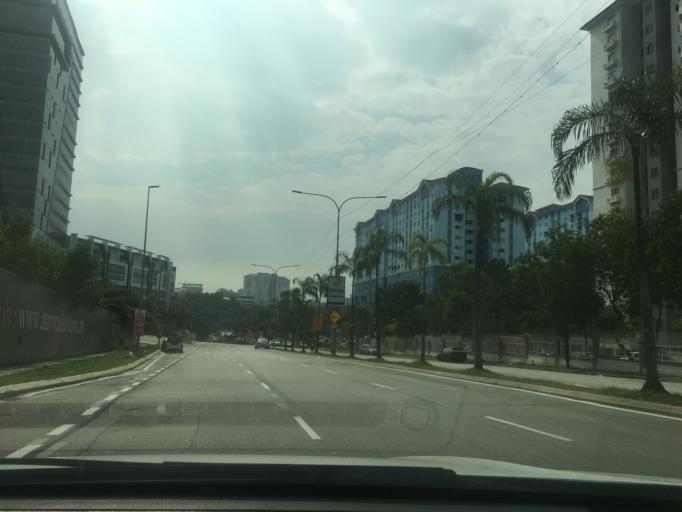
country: MY
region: Selangor
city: Kampong Baharu Balakong
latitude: 3.0550
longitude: 101.6710
